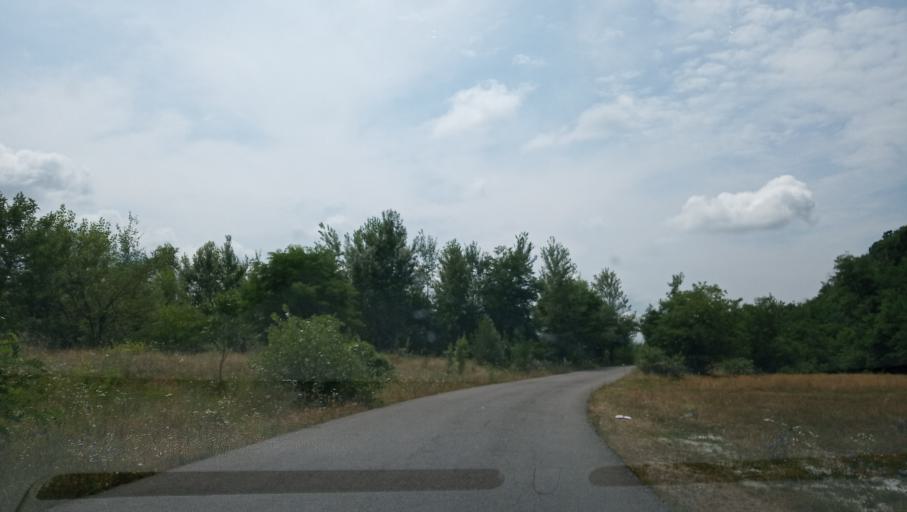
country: RO
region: Gorj
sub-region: Comuna Turcinesti
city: Turcinesti
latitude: 45.1431
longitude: 23.3431
